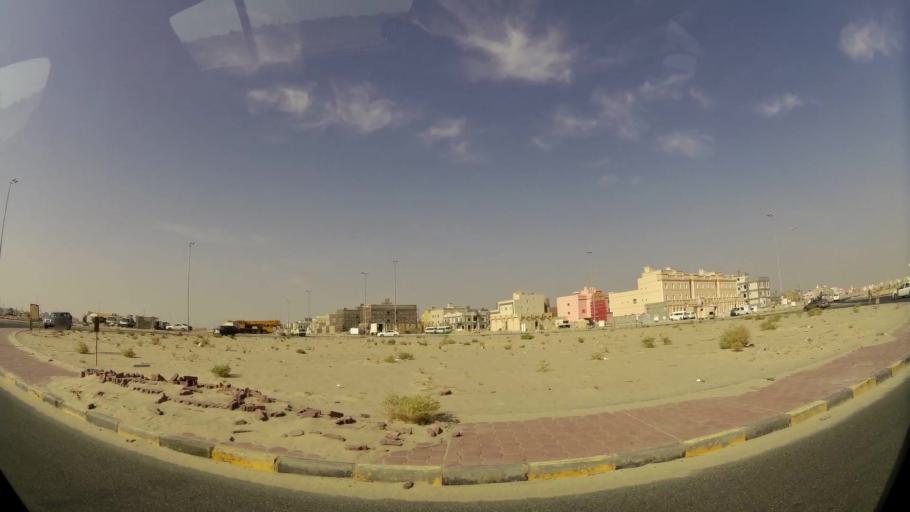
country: KW
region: Al Ahmadi
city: Al Wafrah
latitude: 28.7873
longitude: 48.0690
